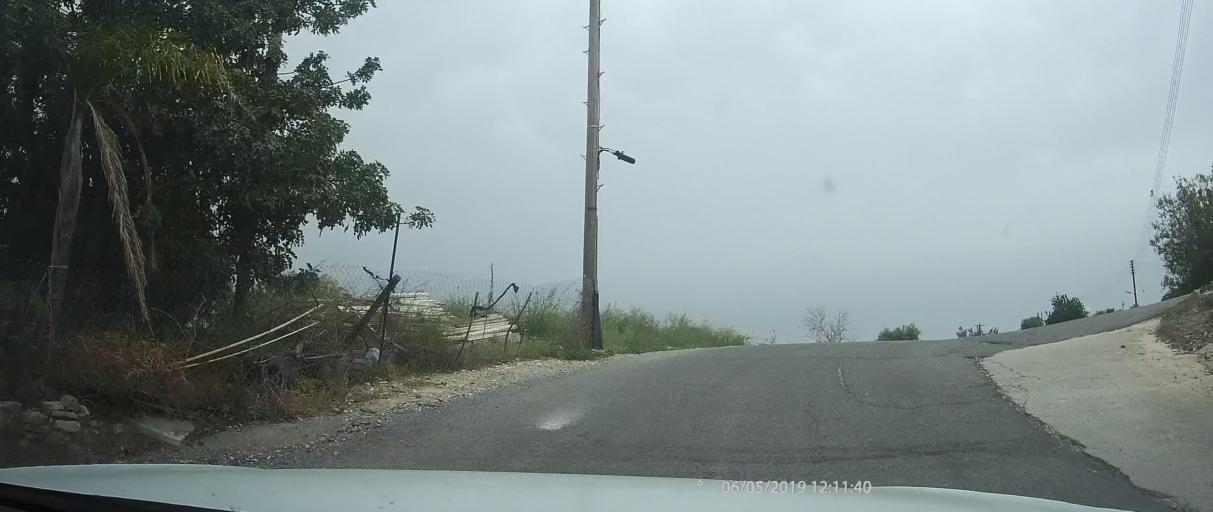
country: CY
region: Pafos
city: Tala
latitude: 34.8388
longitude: 32.4310
